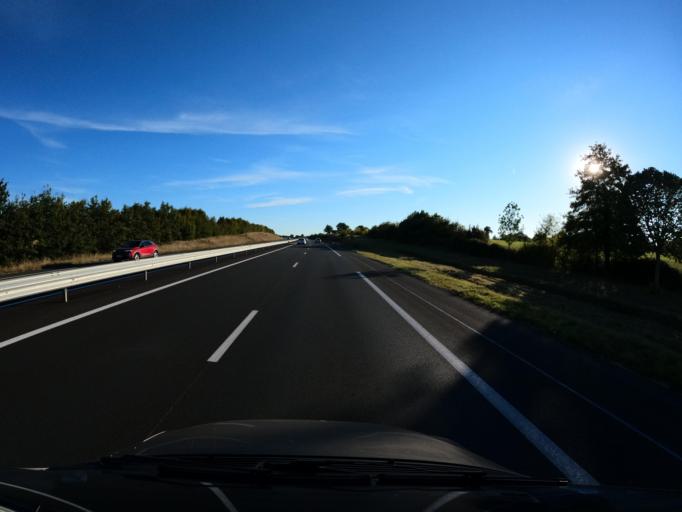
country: FR
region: Pays de la Loire
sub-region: Departement de la Vendee
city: Mortagne-sur-Sevre
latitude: 46.9872
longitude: -0.9170
